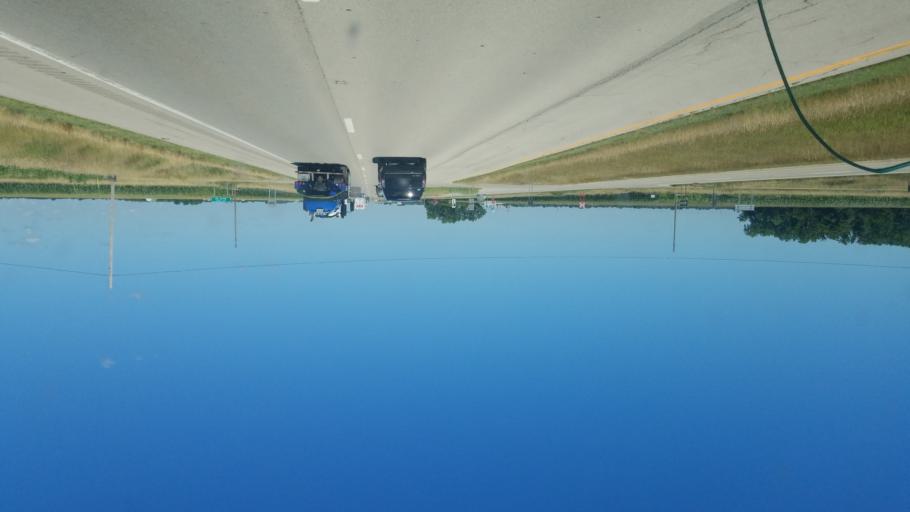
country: US
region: Ohio
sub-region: Van Wert County
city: Van Wert
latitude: 40.8852
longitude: -84.5423
